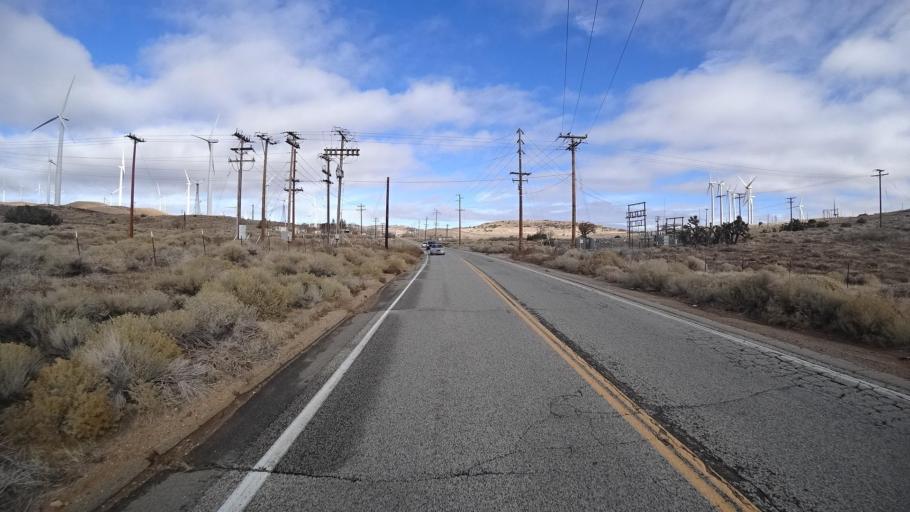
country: US
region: California
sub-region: Kern County
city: Tehachapi
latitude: 35.0315
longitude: -118.3530
